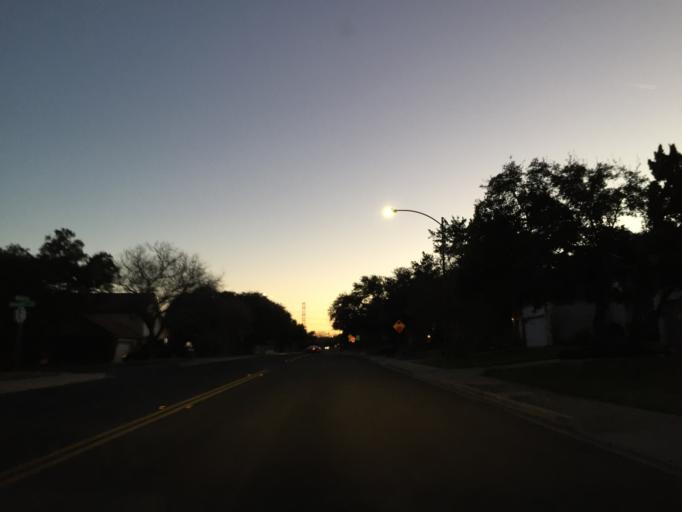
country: US
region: Texas
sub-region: Travis County
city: Wells Branch
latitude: 30.3974
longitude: -97.6953
